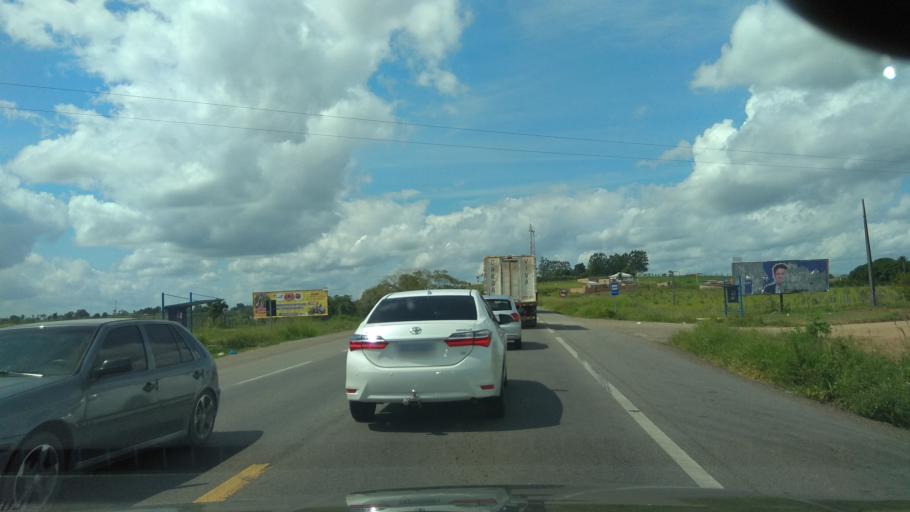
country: BR
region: Bahia
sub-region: Cruz Das Almas
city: Cruz das Almas
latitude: -12.6077
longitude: -39.0663
